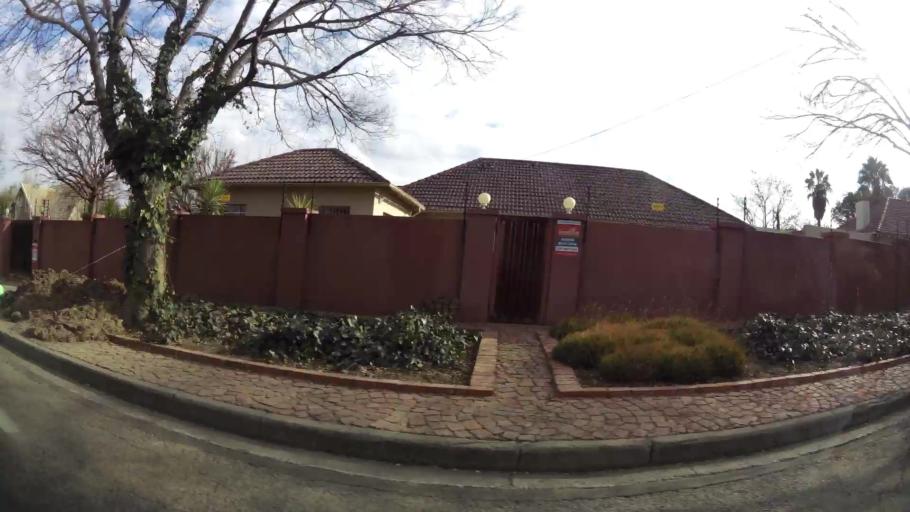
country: ZA
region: Orange Free State
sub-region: Mangaung Metropolitan Municipality
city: Bloemfontein
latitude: -29.0836
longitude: 26.2105
